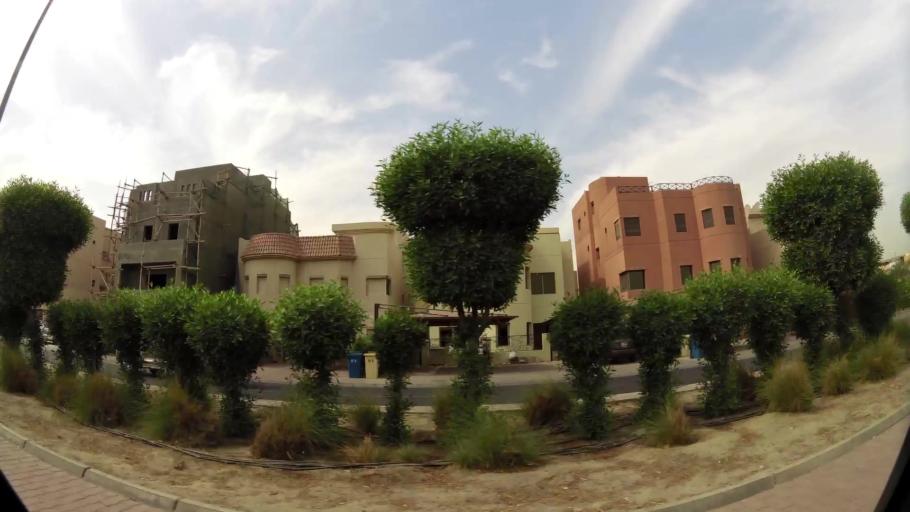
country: KW
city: Bayan
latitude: 29.2796
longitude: 48.0212
